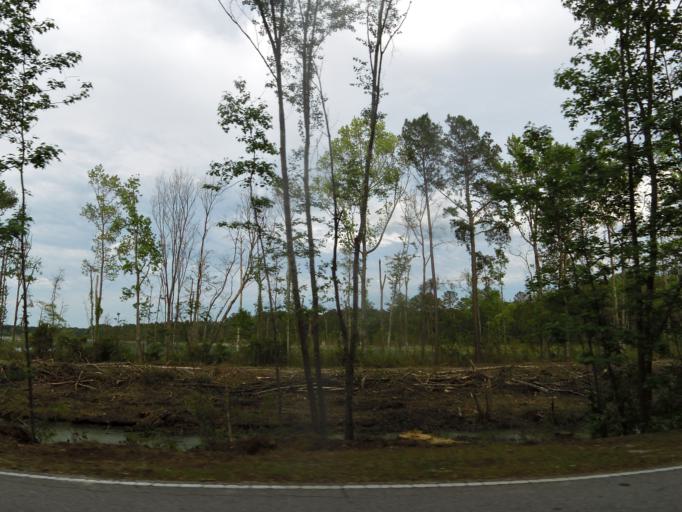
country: US
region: South Carolina
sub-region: Jasper County
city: Hardeeville
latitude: 32.3805
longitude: -81.0968
